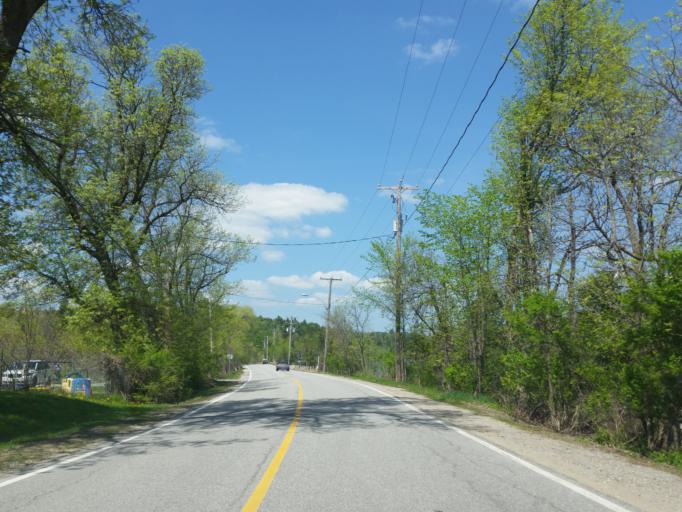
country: CA
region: Quebec
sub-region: Outaouais
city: Wakefield
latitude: 45.6053
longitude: -75.8909
